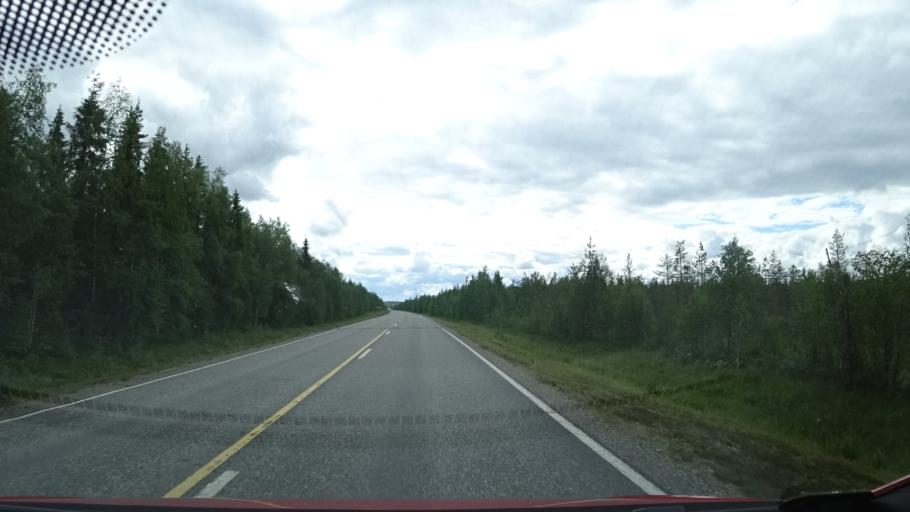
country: FI
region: Lapland
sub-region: Tunturi-Lappi
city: Kittilae
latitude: 67.5909
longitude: 24.9253
